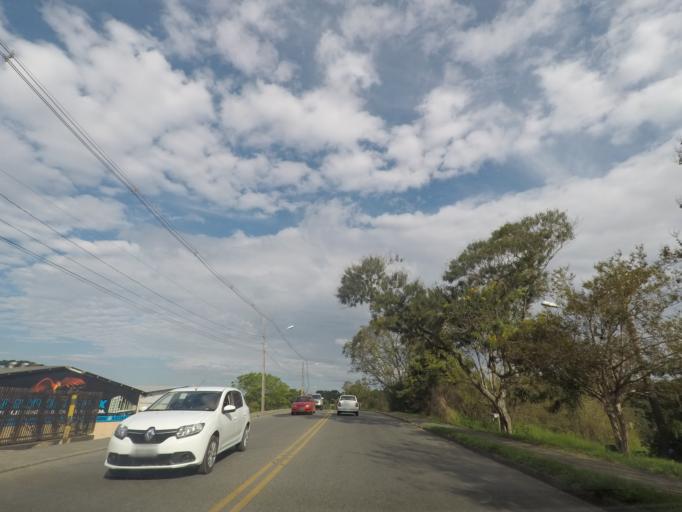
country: BR
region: Parana
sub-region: Sao Jose Dos Pinhais
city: Sao Jose dos Pinhais
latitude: -25.5623
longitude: -49.2910
